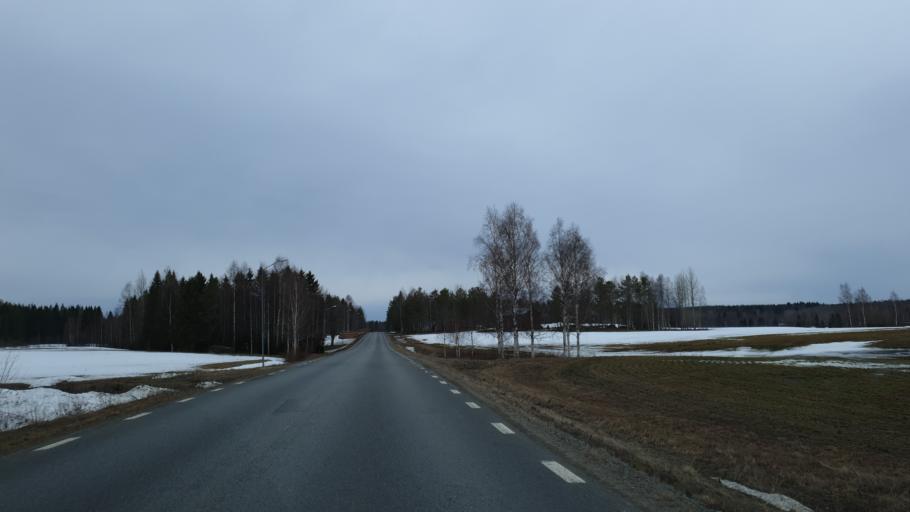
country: SE
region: Vaesterbotten
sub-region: Robertsfors Kommun
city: Robertsfors
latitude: 64.3833
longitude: 20.8978
